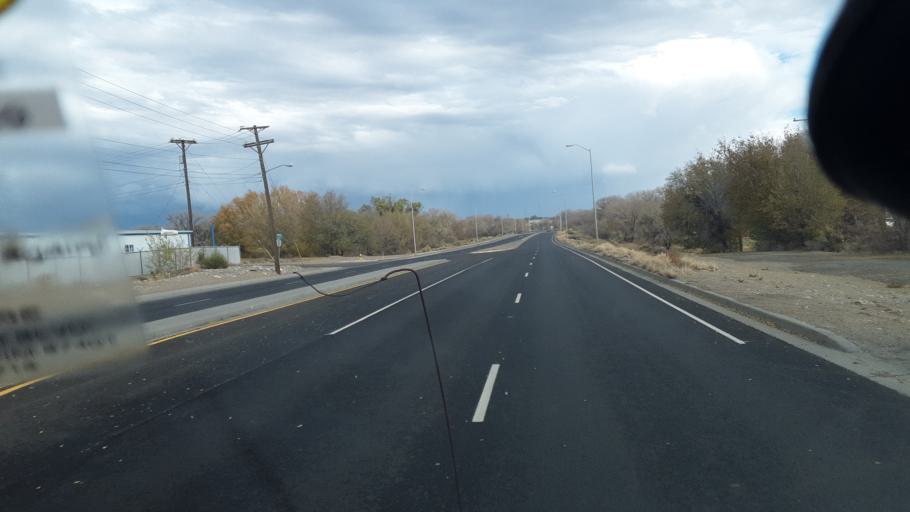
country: US
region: New Mexico
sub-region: San Juan County
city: Farmington
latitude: 36.7192
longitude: -108.2134
